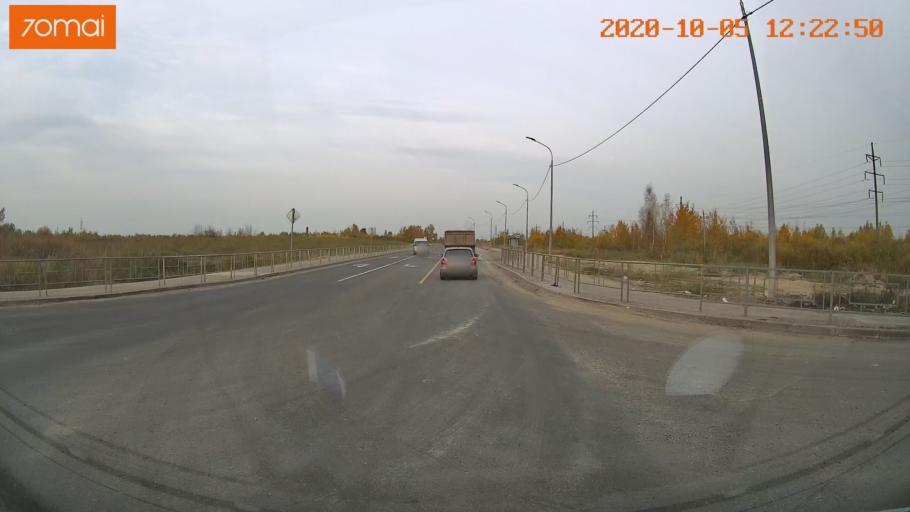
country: RU
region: Ivanovo
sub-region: Gorod Ivanovo
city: Ivanovo
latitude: 56.9764
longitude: 40.9224
